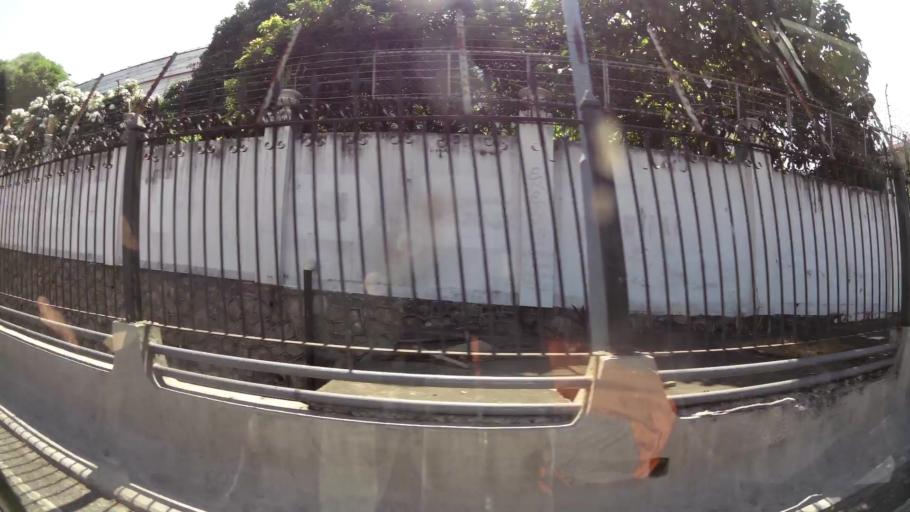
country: EC
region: Guayas
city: Guayaquil
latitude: -2.1834
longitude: -79.8898
